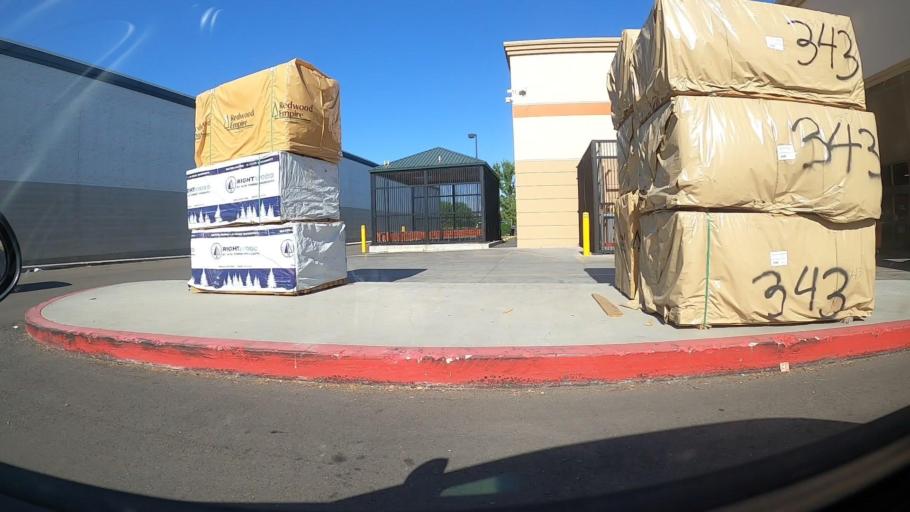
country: US
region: Idaho
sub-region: Ada County
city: Meridian
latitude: 43.5956
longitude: -116.3901
